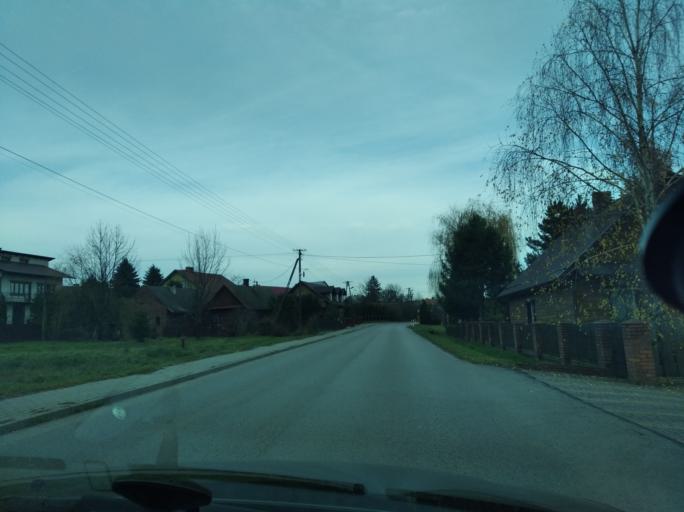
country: PL
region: Subcarpathian Voivodeship
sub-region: Powiat przeworski
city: Debow
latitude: 50.0470
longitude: 22.4606
